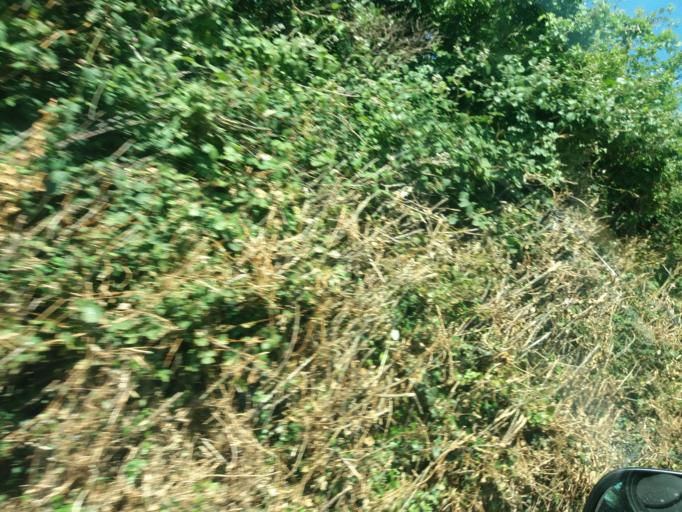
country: IE
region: Leinster
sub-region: Dublin City
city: Finglas
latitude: 53.4375
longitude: -6.3109
